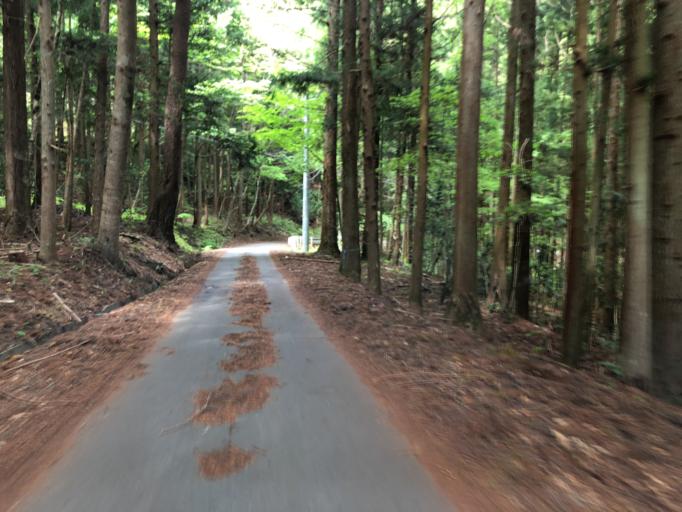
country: JP
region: Miyagi
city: Marumori
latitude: 37.7291
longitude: 140.8080
